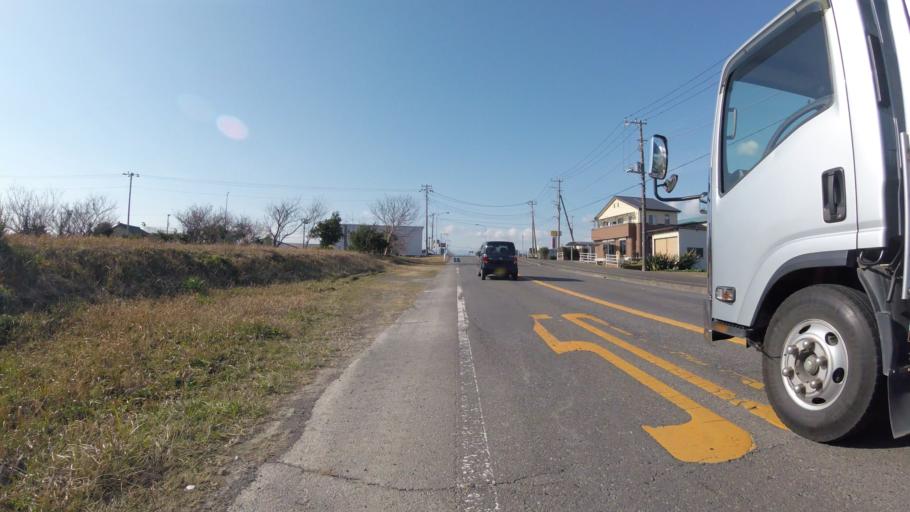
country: JP
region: Shizuoka
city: Fuji
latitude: 35.1501
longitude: 138.7657
